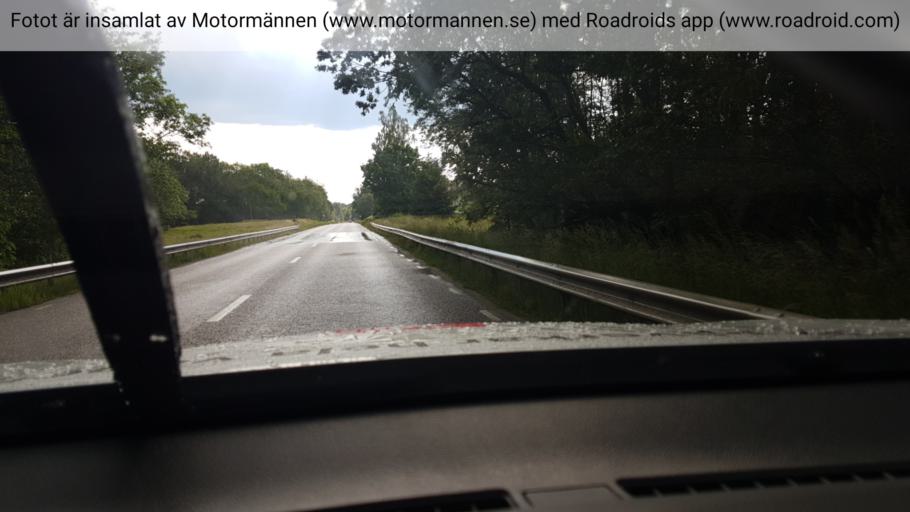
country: SE
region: Vaestra Goetaland
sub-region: Hjo Kommun
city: Hjo
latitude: 58.2321
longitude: 14.2192
